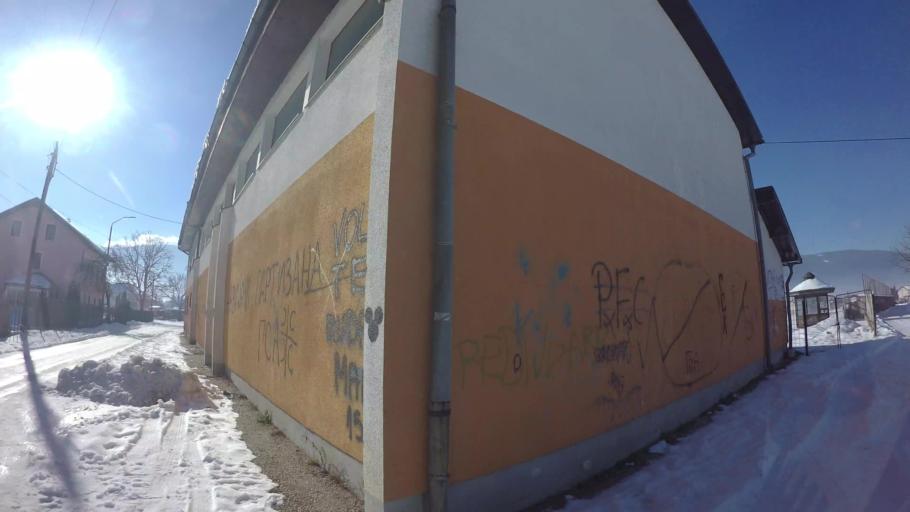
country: BA
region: Federation of Bosnia and Herzegovina
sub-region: Kanton Sarajevo
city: Sarajevo
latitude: 43.7988
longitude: 18.3473
